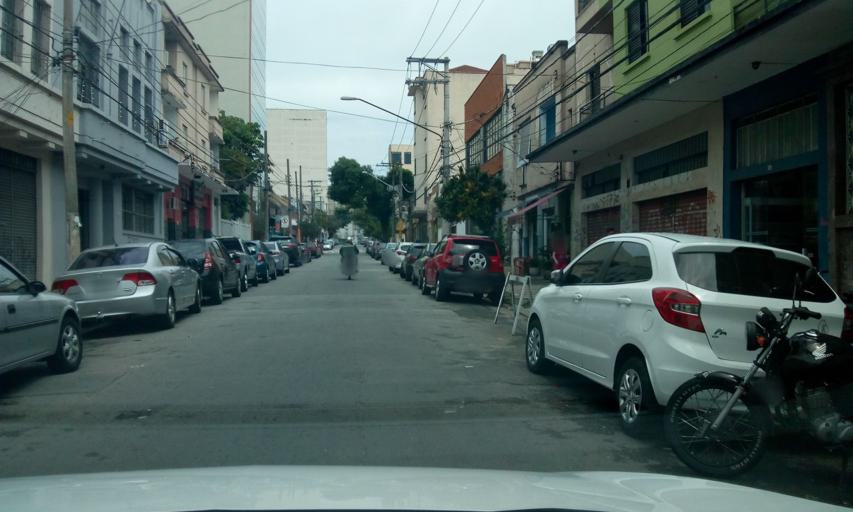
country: BR
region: Sao Paulo
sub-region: Sao Paulo
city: Sao Paulo
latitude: -23.5285
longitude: -46.6577
